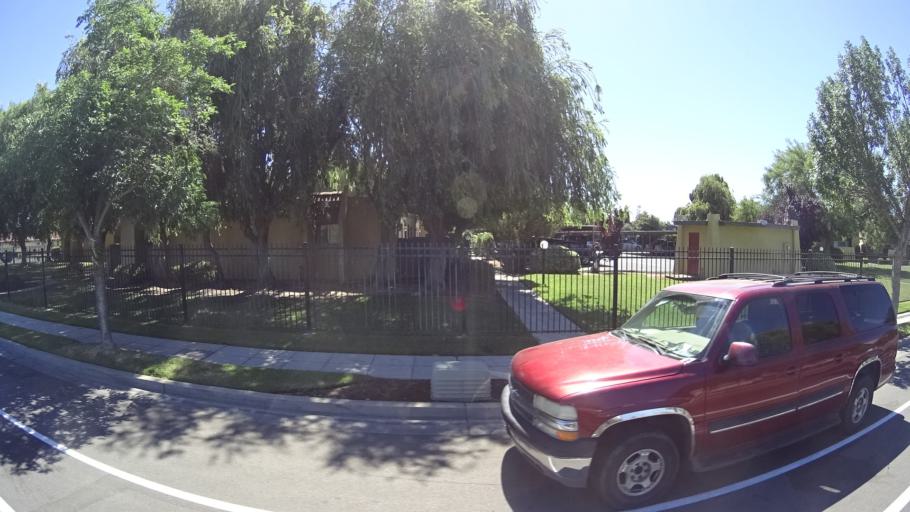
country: US
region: California
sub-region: Fresno County
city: Fresno
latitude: 36.7948
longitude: -119.8353
